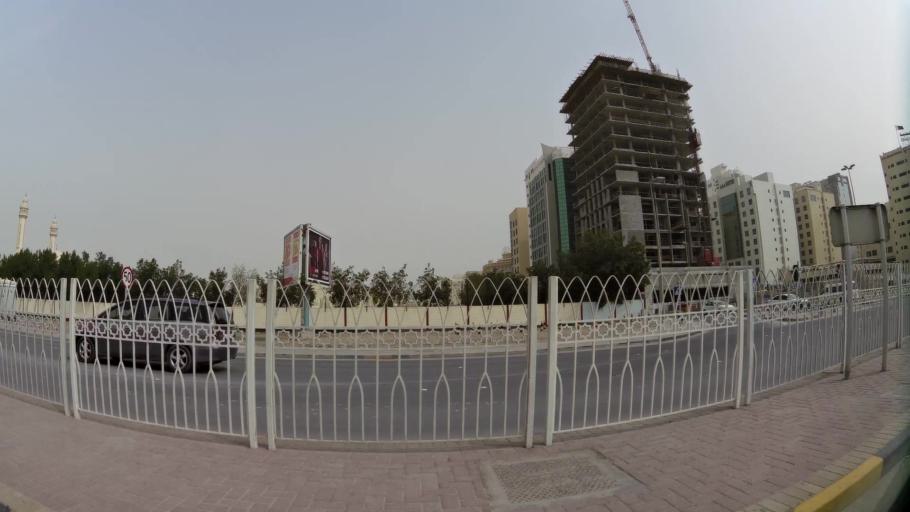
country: BH
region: Manama
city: Manama
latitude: 26.2167
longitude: 50.6007
